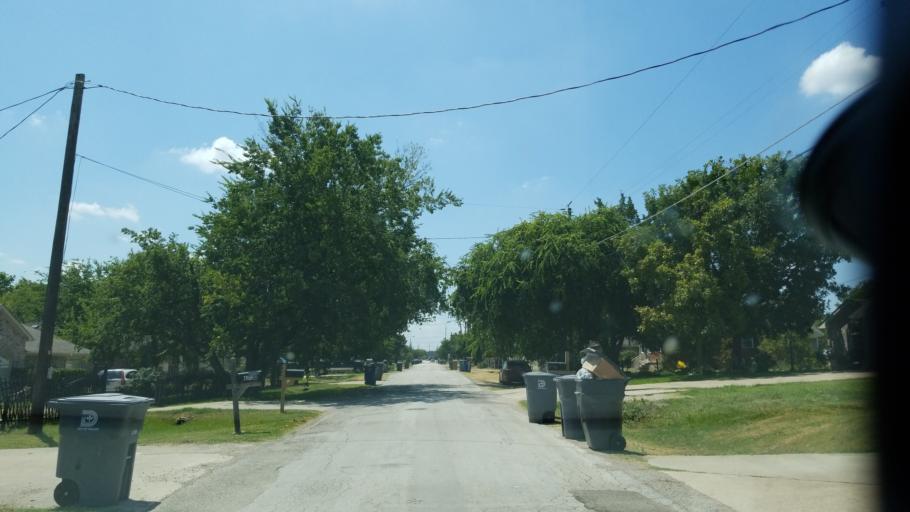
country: US
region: Texas
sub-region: Dallas County
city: Duncanville
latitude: 32.6663
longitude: -96.8841
